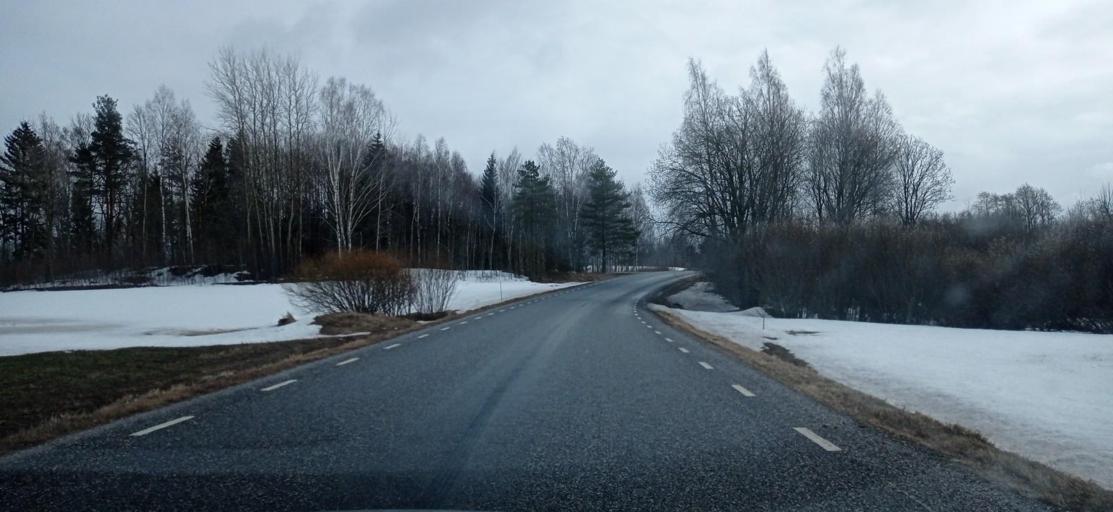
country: EE
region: Tartu
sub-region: UElenurme vald
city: Ulenurme
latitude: 58.0780
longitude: 26.6935
